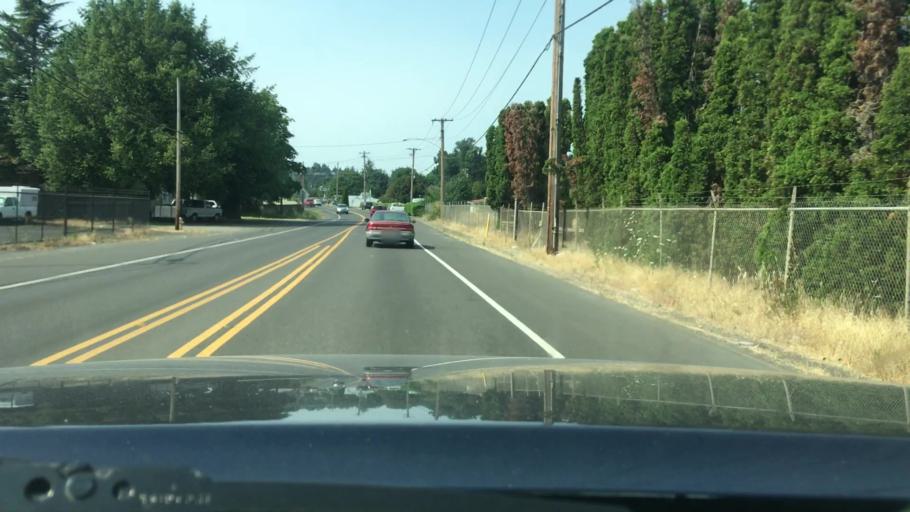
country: US
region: Oregon
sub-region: Lane County
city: Springfield
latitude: 44.0360
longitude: -123.0270
